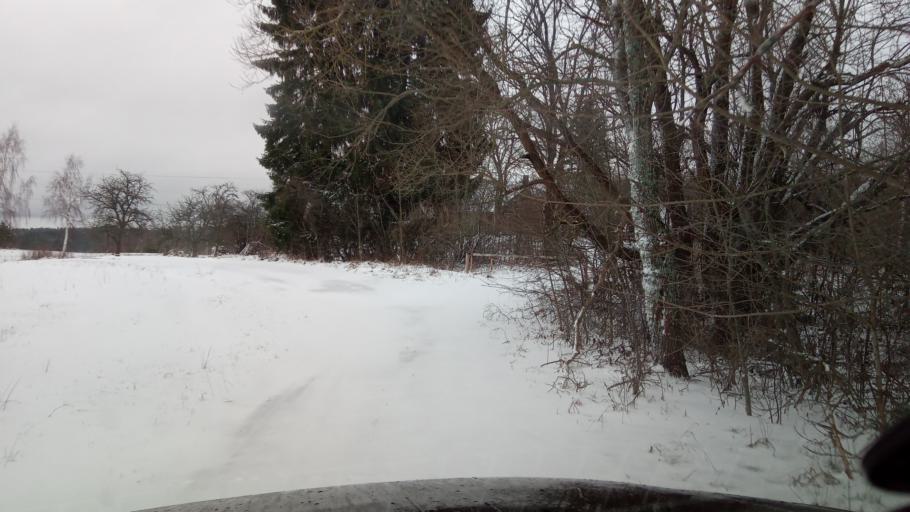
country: LT
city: Zarasai
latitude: 55.6390
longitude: 25.9801
